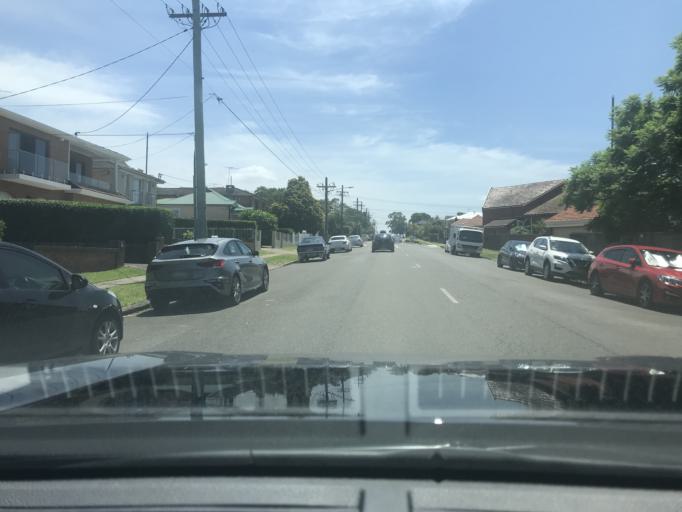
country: AU
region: New South Wales
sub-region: Canada Bay
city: Concord
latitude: -33.8624
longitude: 151.1005
